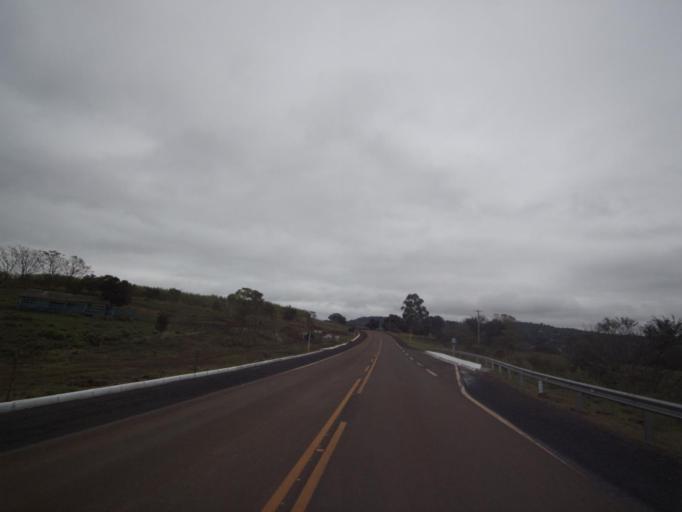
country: AR
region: Misiones
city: El Soberbio
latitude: -27.2870
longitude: -54.1866
